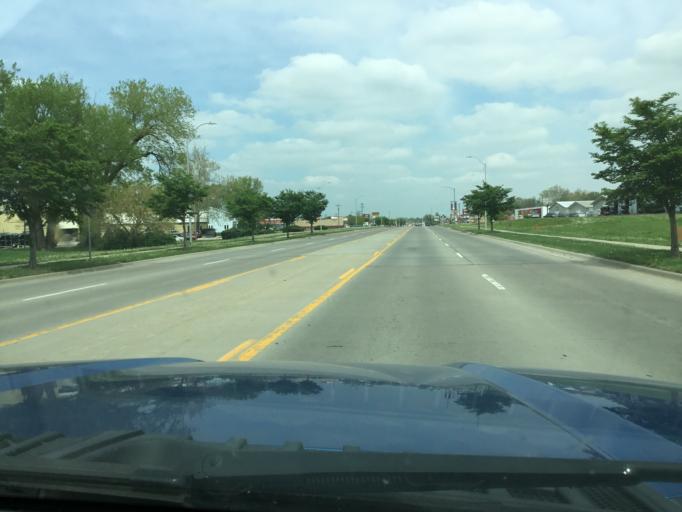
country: US
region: Kansas
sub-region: Shawnee County
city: Topeka
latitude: 39.0778
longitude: -95.6684
